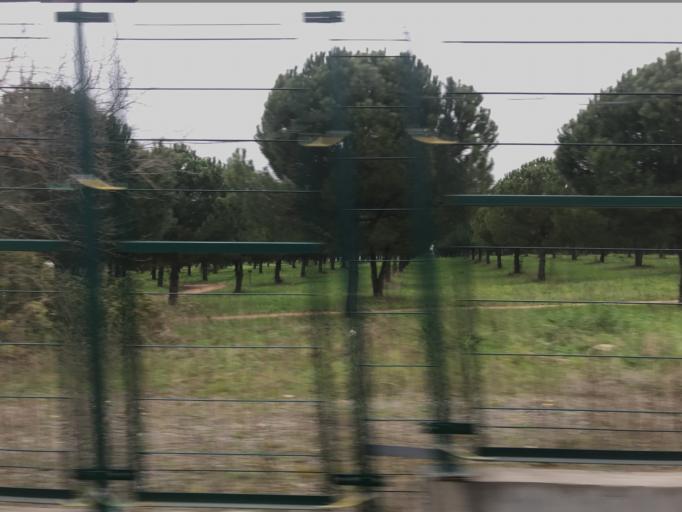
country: TR
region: Istanbul
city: Icmeler
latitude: 40.8105
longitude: 29.3482
